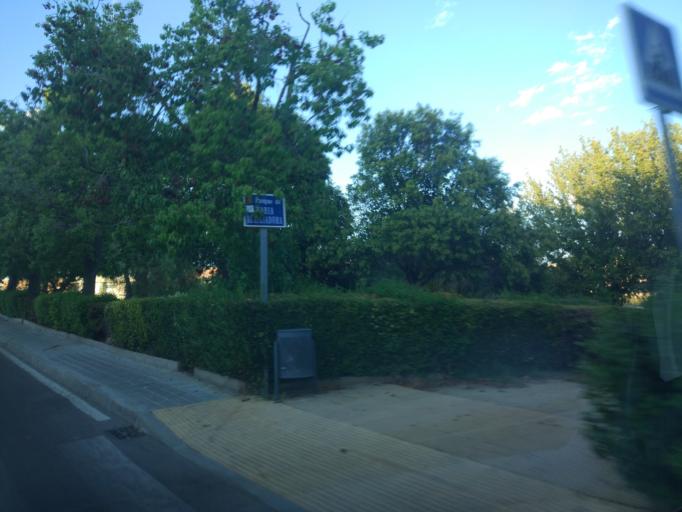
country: ES
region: Andalusia
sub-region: Provincia de Jaen
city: Jaen
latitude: 37.7869
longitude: -3.7796
